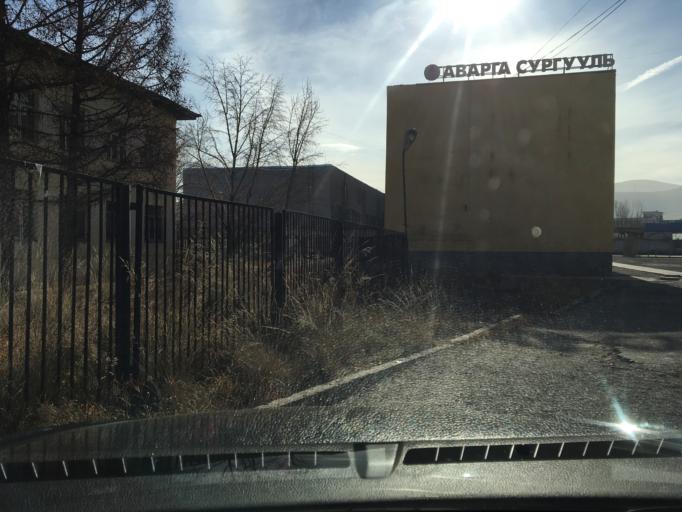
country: MN
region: Ulaanbaatar
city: Ulaanbaatar
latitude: 47.8967
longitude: 106.8911
